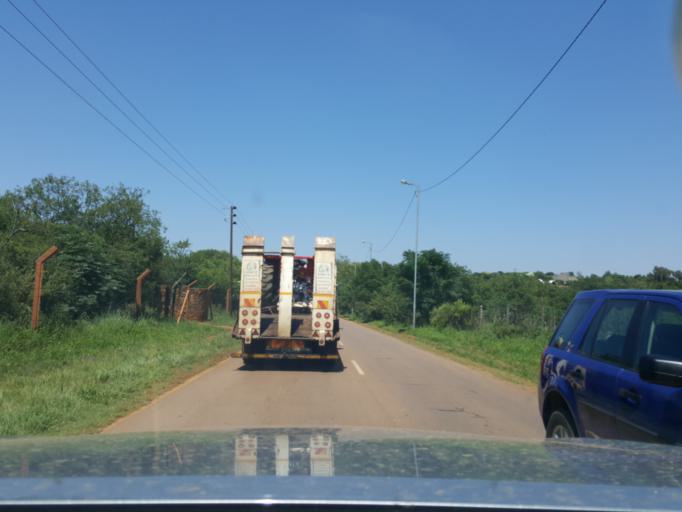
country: ZA
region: Gauteng
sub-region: City of Tshwane Metropolitan Municipality
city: Pretoria
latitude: -25.6623
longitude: 28.3103
